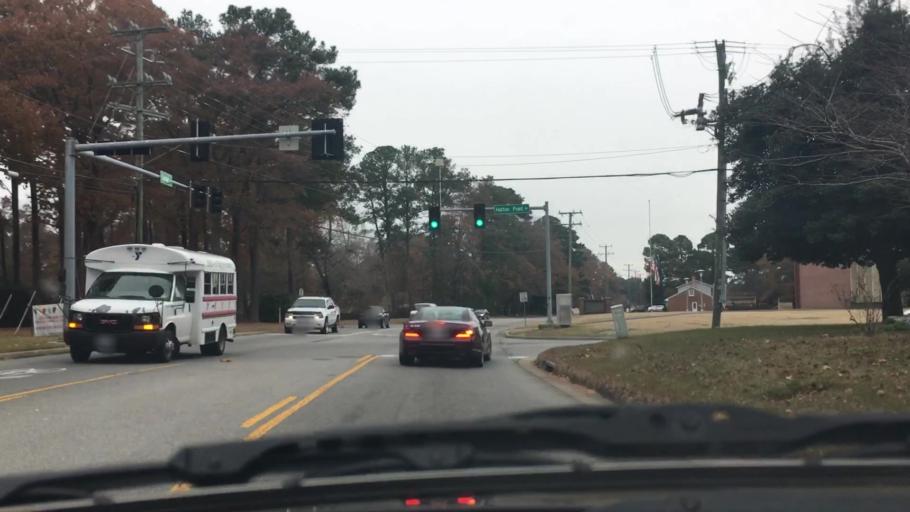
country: US
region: Virginia
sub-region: City of Portsmouth
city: Portsmouth Heights
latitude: 36.8555
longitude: -76.3787
